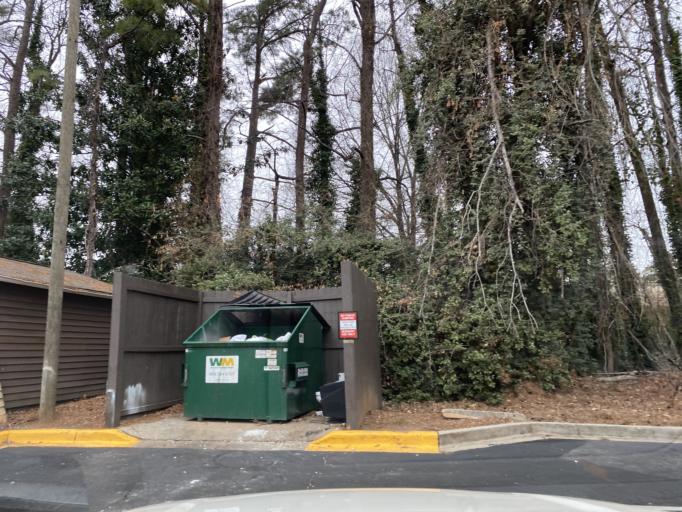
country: US
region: Georgia
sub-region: Cobb County
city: Fair Oaks
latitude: 33.9222
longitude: -84.5758
